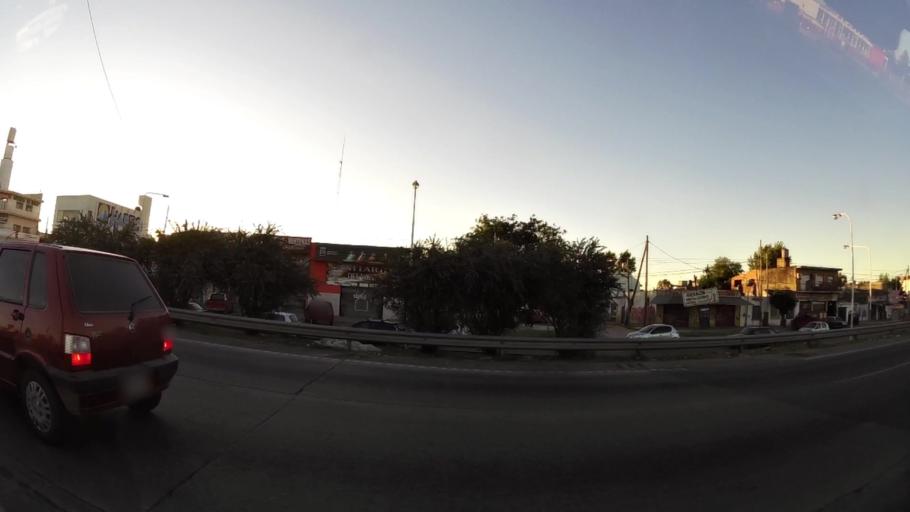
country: AR
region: Buenos Aires
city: Pontevedra
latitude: -34.7679
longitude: -58.6186
